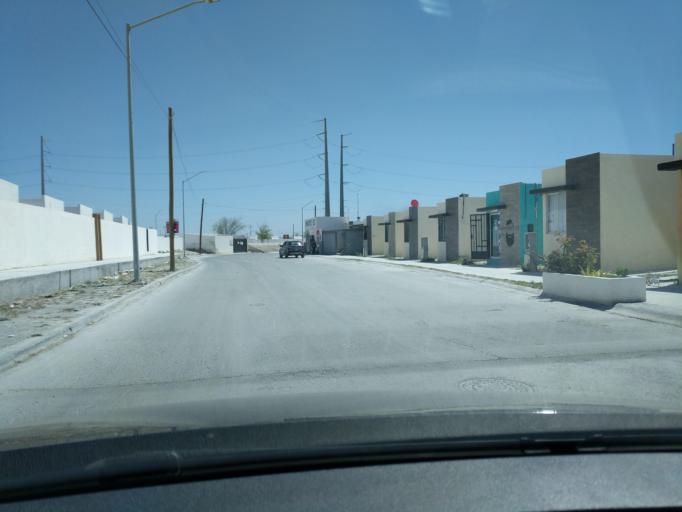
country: MX
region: Nuevo Leon
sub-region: Apodaca
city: Artemio Trevino
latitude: 25.8405
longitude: -100.1393
